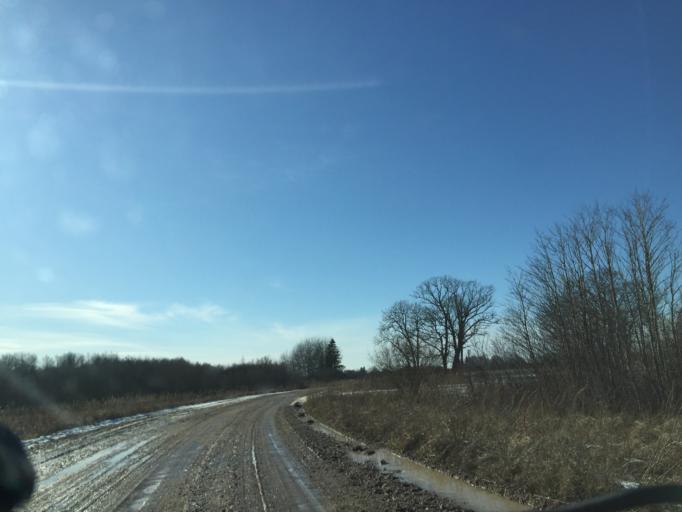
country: LV
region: Ventspils Rajons
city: Piltene
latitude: 57.2678
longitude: 21.6805
